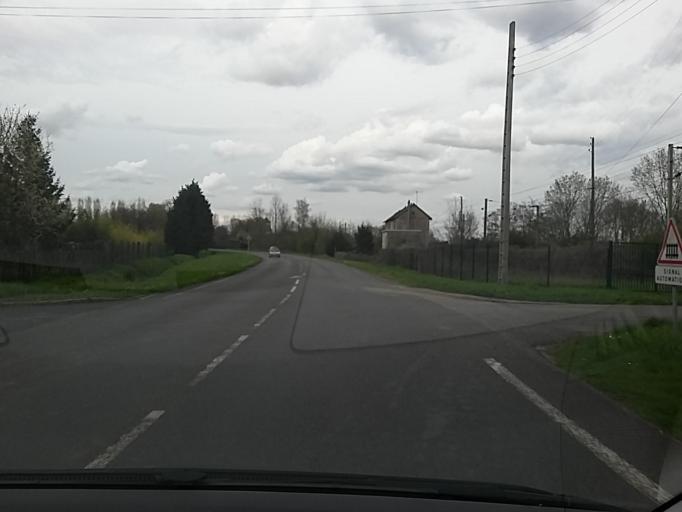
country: FR
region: Picardie
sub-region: Departement de l'Oise
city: Longueil-Sainte-Marie
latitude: 49.3465
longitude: 2.7367
